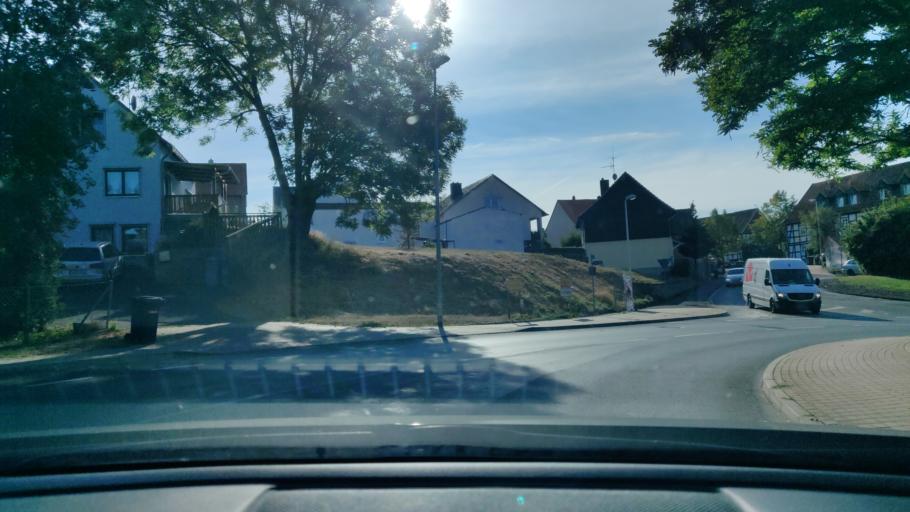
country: DE
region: Hesse
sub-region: Regierungsbezirk Kassel
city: Bad Wildungen
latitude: 51.1282
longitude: 9.1269
